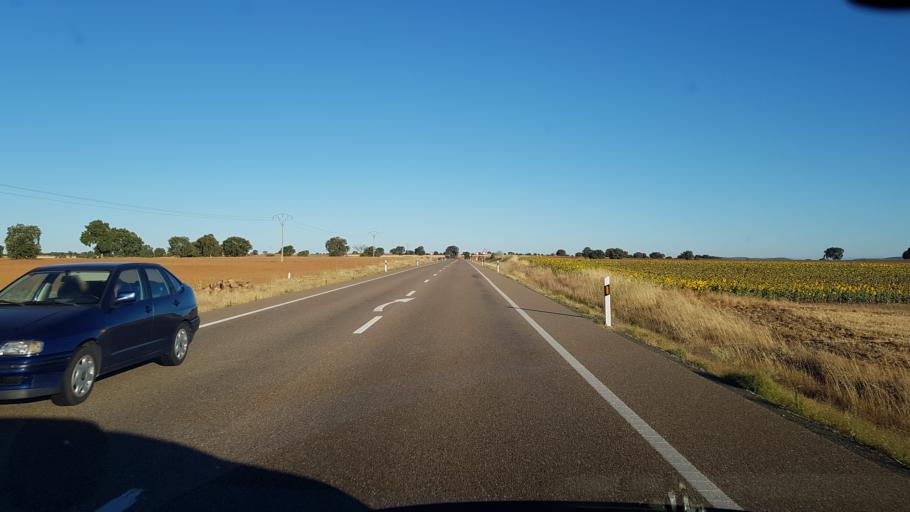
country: ES
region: Castille and Leon
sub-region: Provincia de Zamora
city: Palacios del Pan
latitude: 41.5455
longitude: -5.8822
